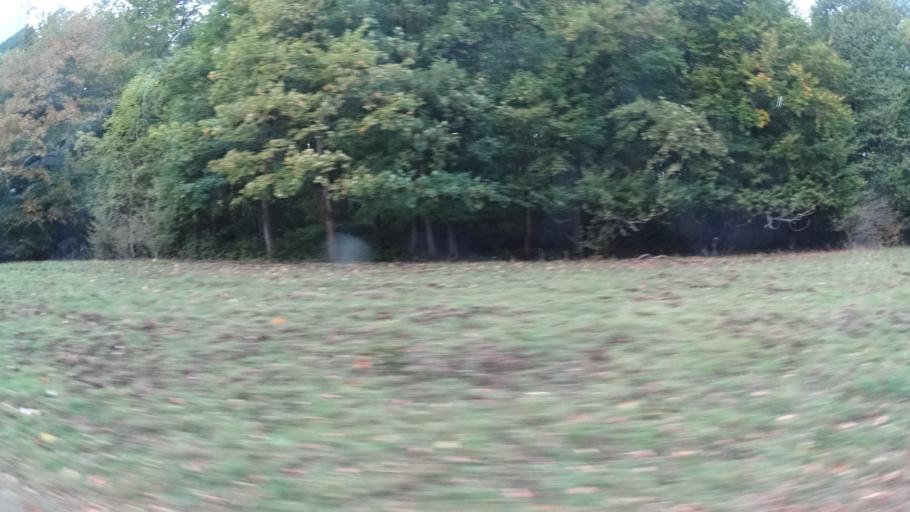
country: DE
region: Thuringia
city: Altersbach
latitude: 50.7297
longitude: 10.5206
